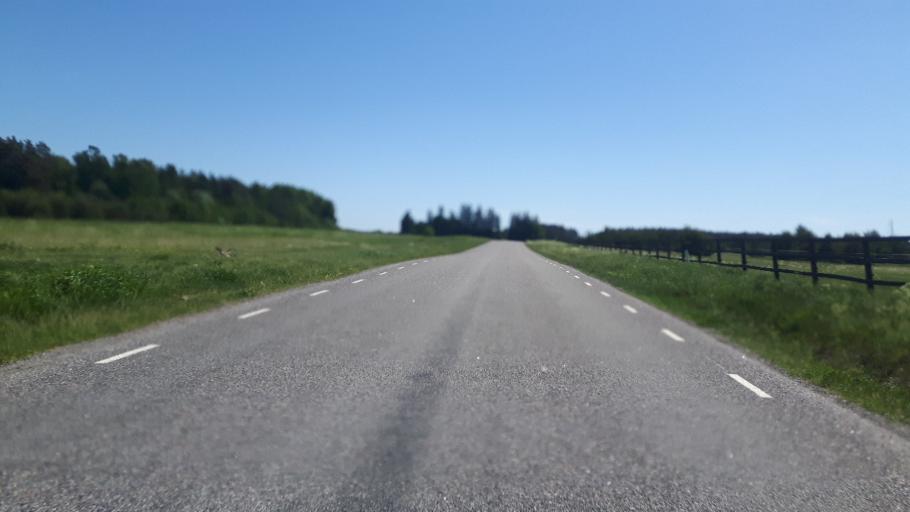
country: EE
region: Raplamaa
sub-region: Kohila vald
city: Kohila
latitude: 59.1987
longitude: 24.6948
